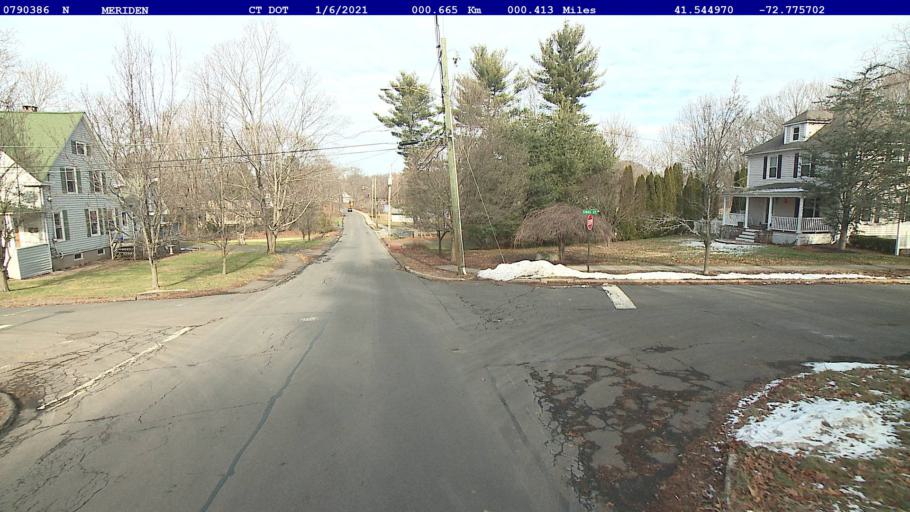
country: US
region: Connecticut
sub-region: New Haven County
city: Meriden
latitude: 41.5450
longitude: -72.7757
